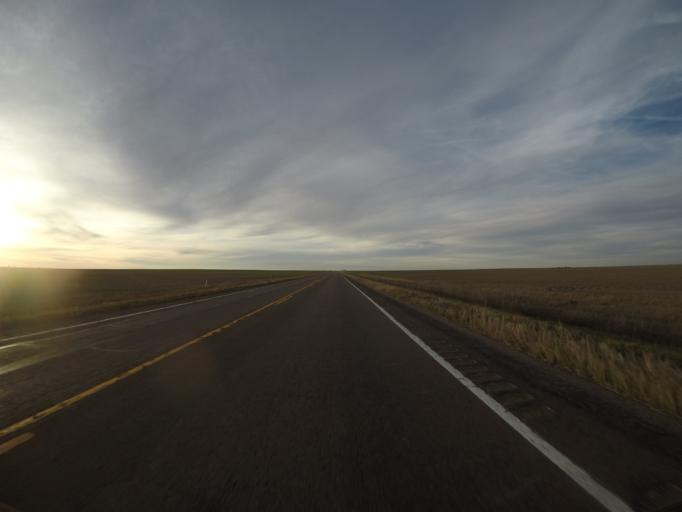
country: US
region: Colorado
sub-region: Washington County
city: Akron
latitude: 39.7299
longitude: -103.1641
